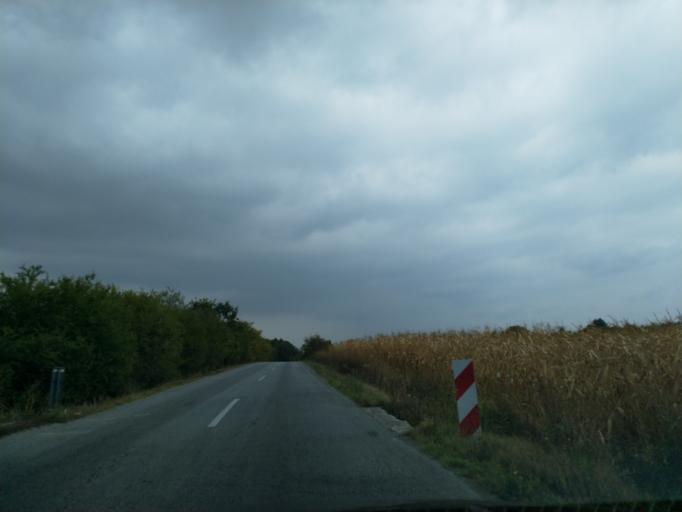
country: RS
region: Central Serbia
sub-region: Pomoravski Okrug
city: Jagodina
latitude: 44.0200
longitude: 21.1963
